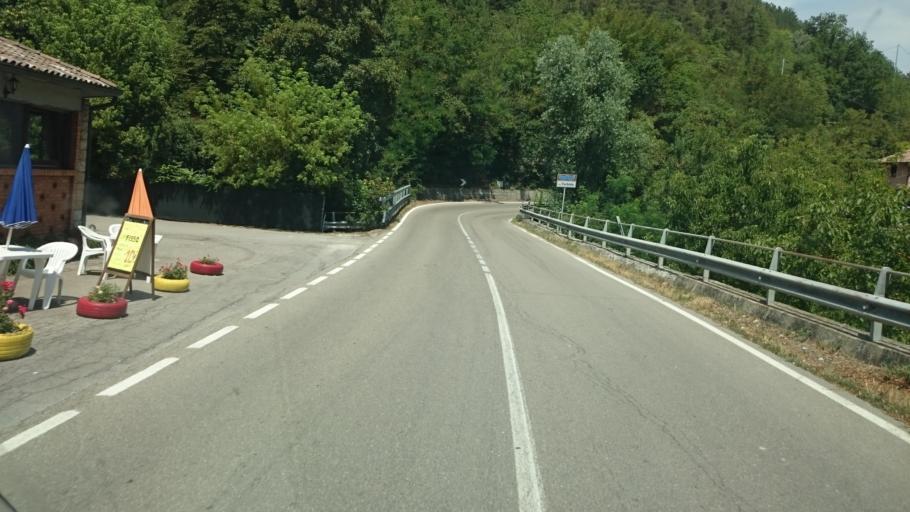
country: IT
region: Emilia-Romagna
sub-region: Provincia di Reggio Emilia
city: Casina
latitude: 44.5412
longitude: 10.5210
